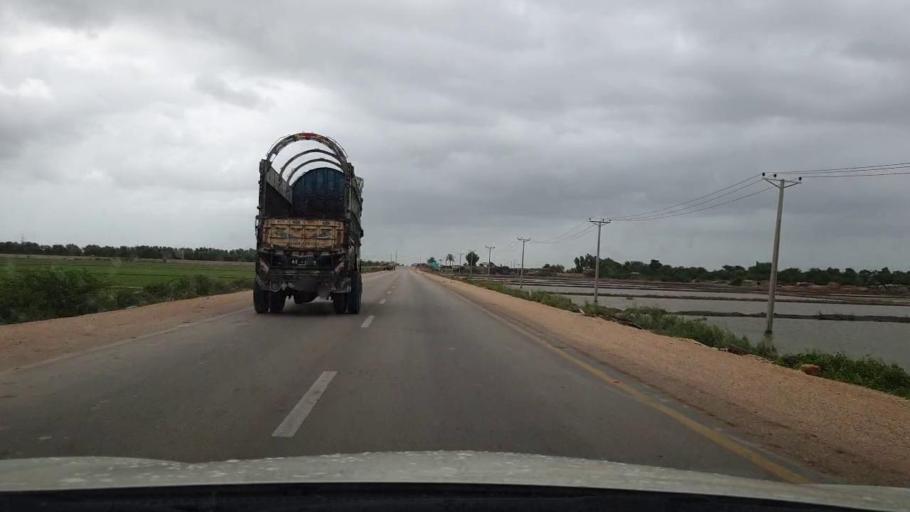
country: PK
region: Sindh
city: Badin
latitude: 24.6555
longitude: 68.7243
